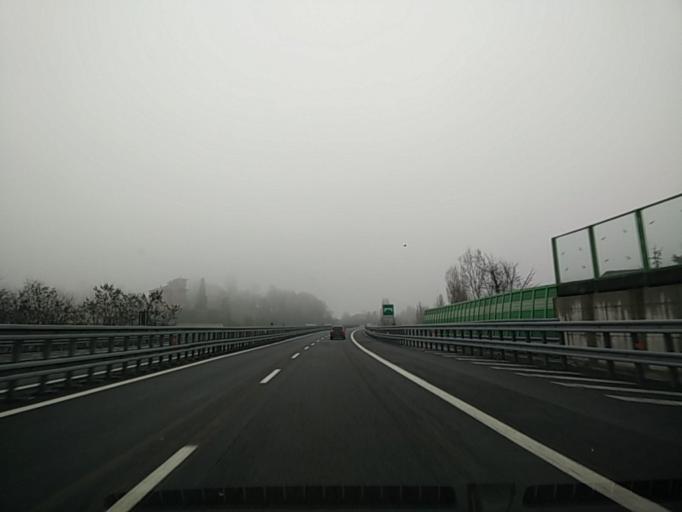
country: IT
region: Piedmont
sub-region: Provincia di Asti
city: Asti
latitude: 44.9172
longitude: 8.2058
